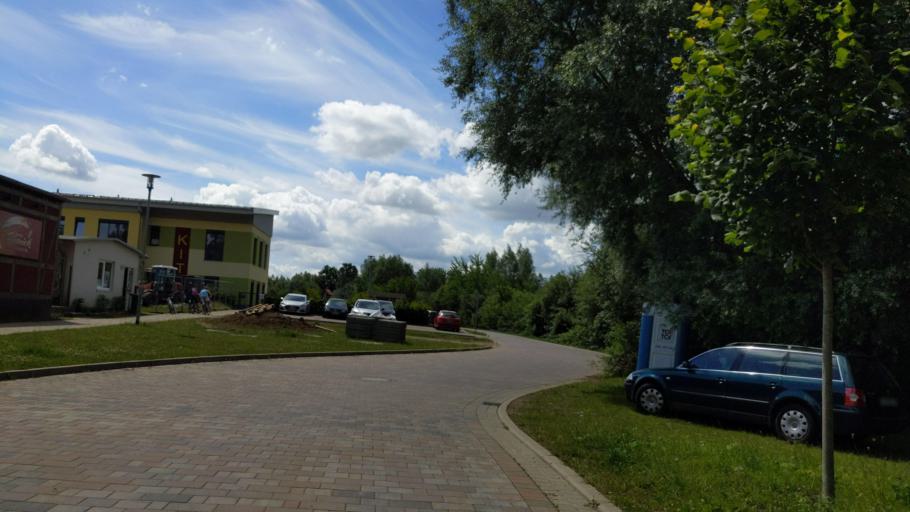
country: DE
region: Mecklenburg-Vorpommern
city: Dassow
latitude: 53.9069
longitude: 10.9798
